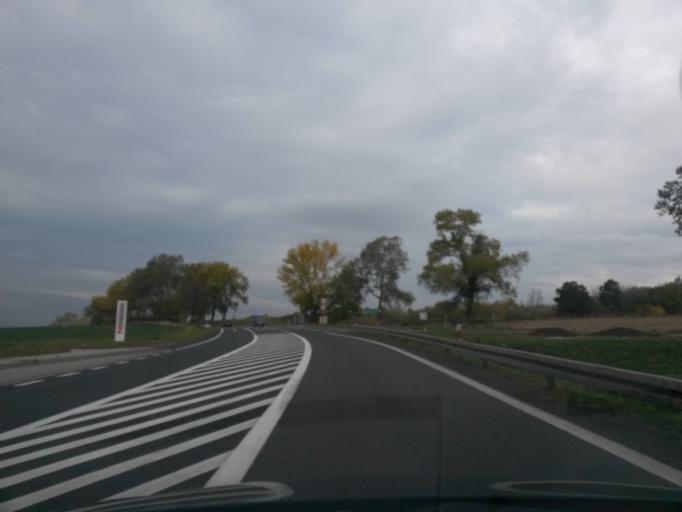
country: PL
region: Lower Silesian Voivodeship
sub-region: Powiat dzierzoniowski
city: Niemcza
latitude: 50.6696
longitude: 16.8314
